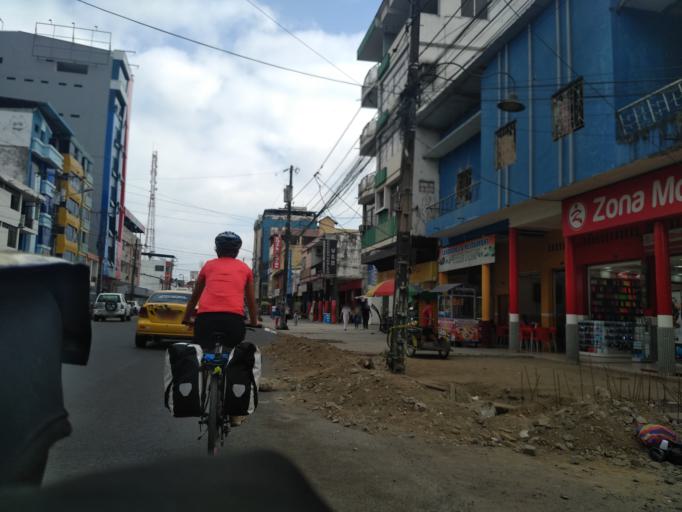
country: EC
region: Los Rios
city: Quevedo
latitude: -1.0283
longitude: -79.4680
